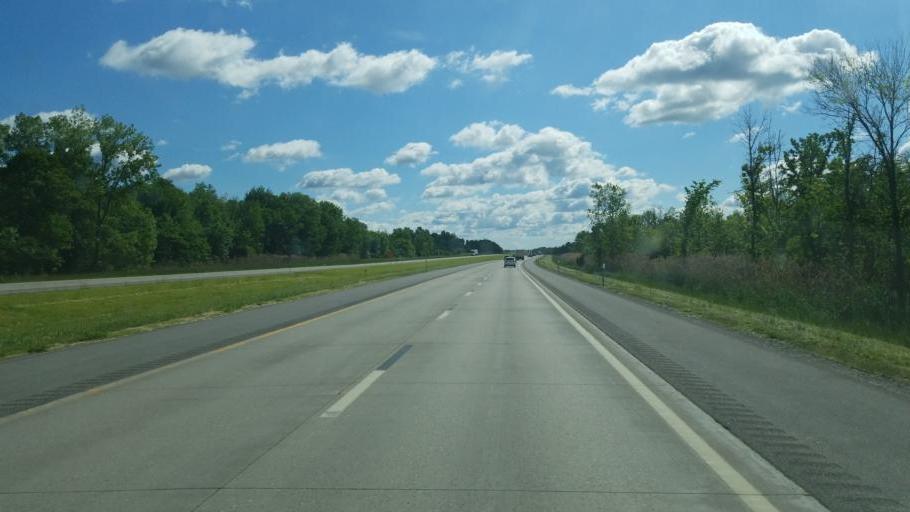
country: US
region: New York
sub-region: Onondaga County
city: Jordan
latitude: 43.0799
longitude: -76.4614
